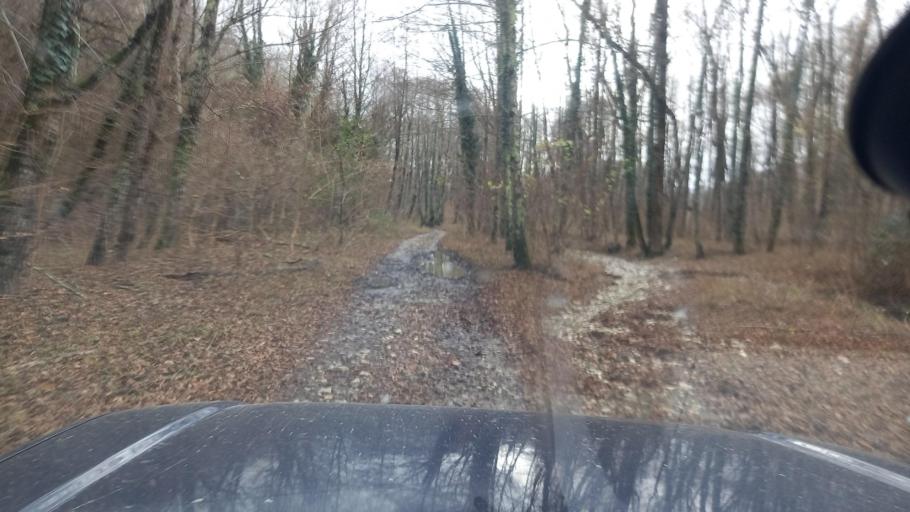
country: RU
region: Krasnodarskiy
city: Pshada
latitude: 44.4871
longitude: 38.4128
